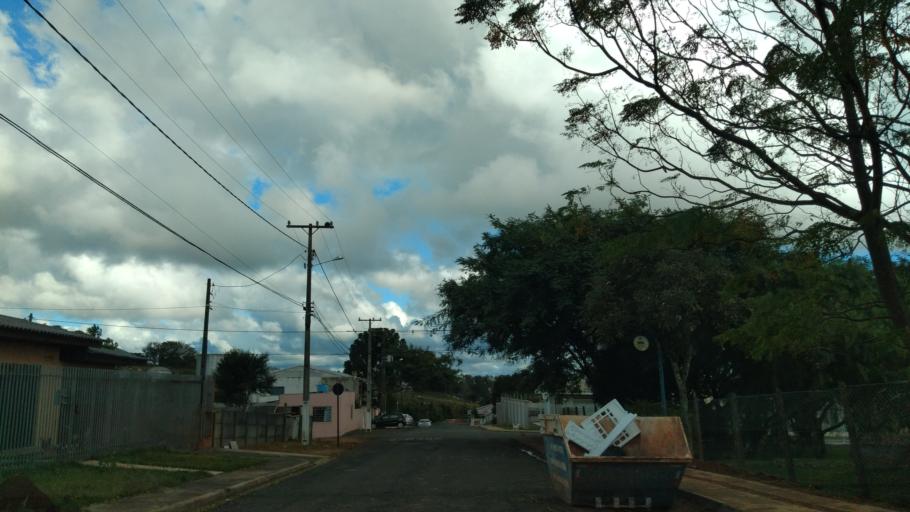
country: BR
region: Parana
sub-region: Guarapuava
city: Guarapuava
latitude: -25.3957
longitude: -51.4885
